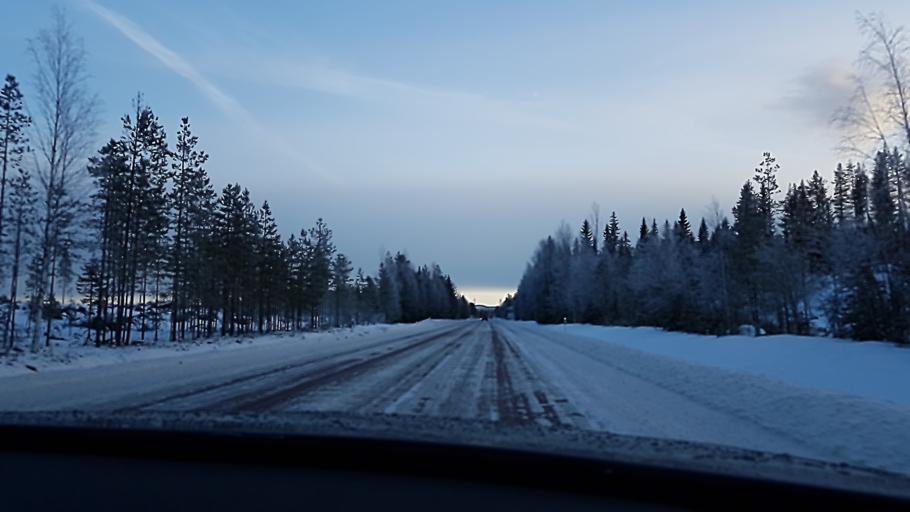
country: SE
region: Jaemtland
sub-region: Bergs Kommun
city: Hoverberg
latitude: 62.4964
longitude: 14.4641
